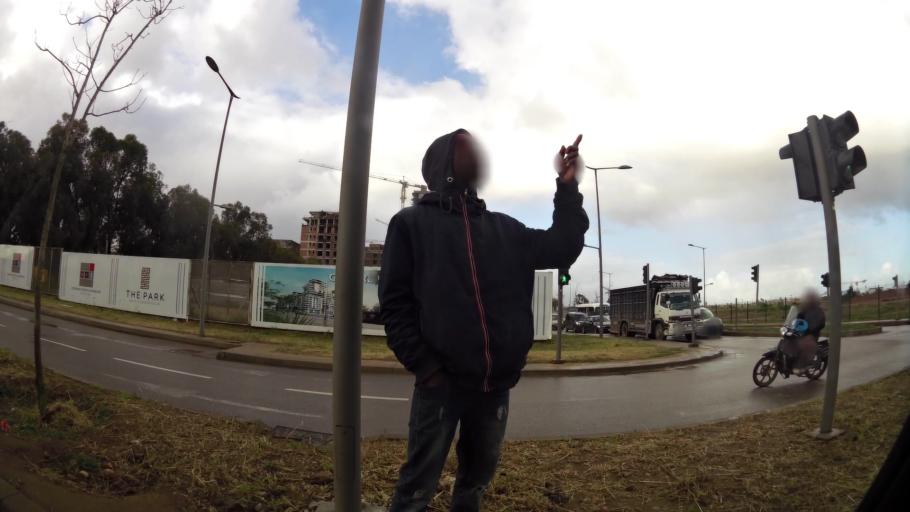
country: MA
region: Grand Casablanca
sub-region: Casablanca
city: Casablanca
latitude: 33.5626
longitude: -7.6547
